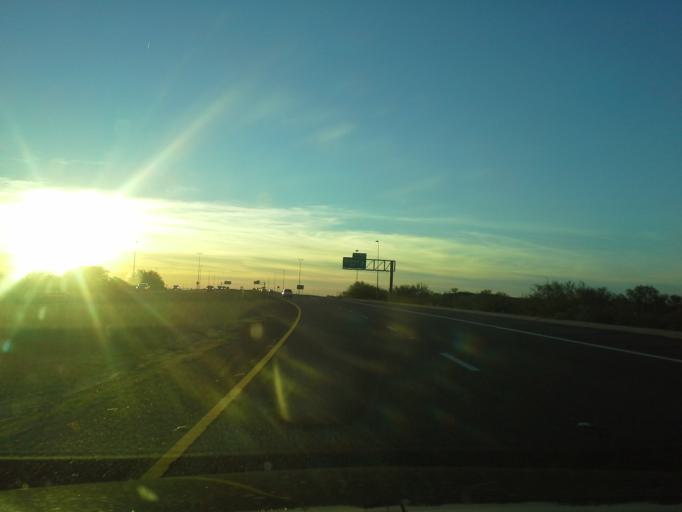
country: US
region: Arizona
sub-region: Pinal County
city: Apache Junction
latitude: 33.3873
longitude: -111.5042
